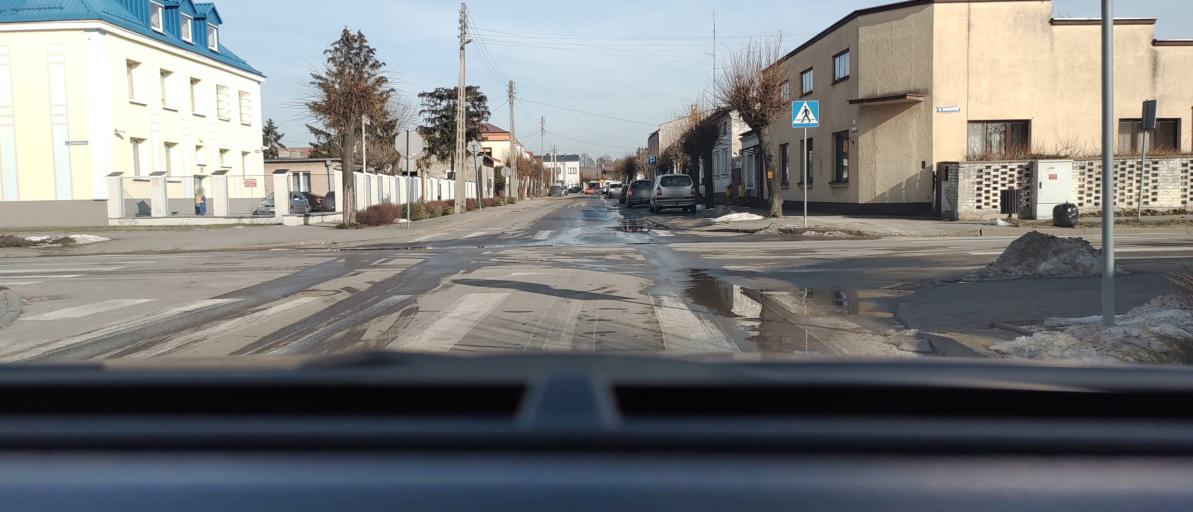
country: PL
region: Masovian Voivodeship
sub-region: Powiat bialobrzeski
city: Bialobrzegi
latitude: 51.6475
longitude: 20.9526
